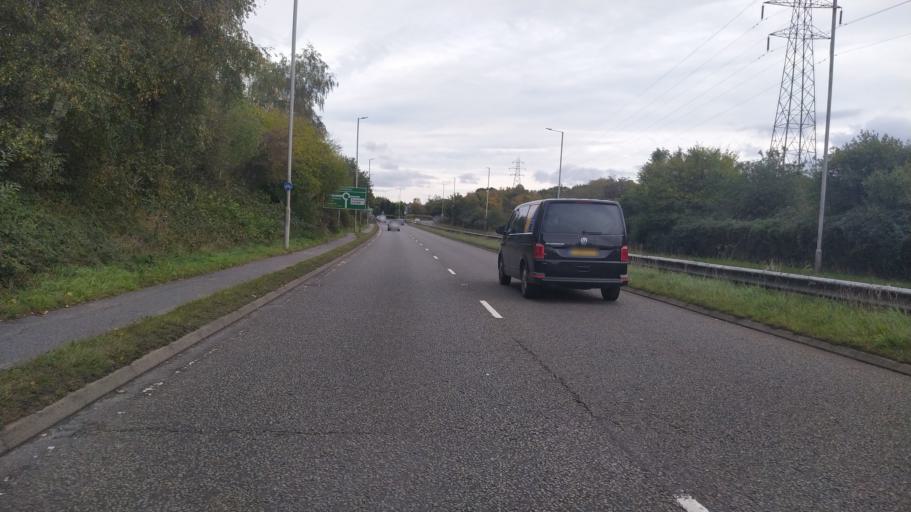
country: GB
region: England
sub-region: Dorset
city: Parkstone
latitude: 50.7521
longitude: -1.9397
